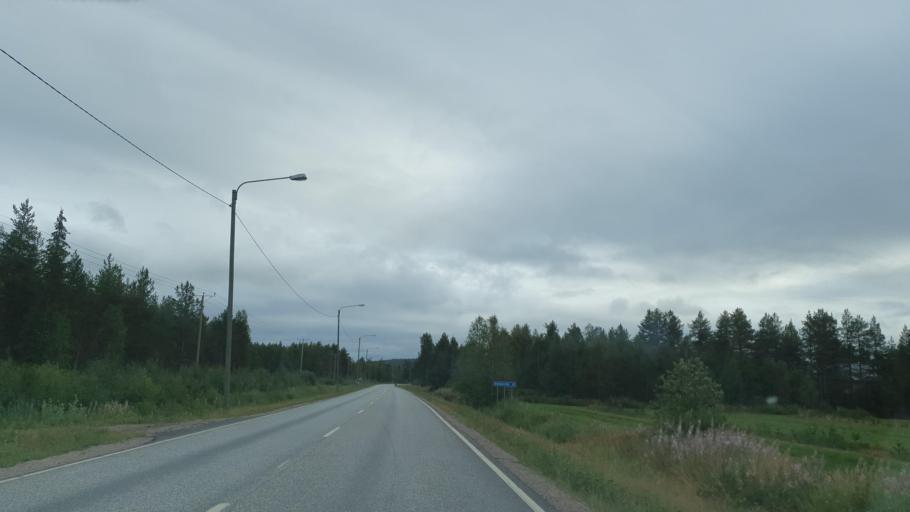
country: FI
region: Lapland
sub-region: Rovaniemi
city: Rovaniemi
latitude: 66.7151
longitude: 25.4521
